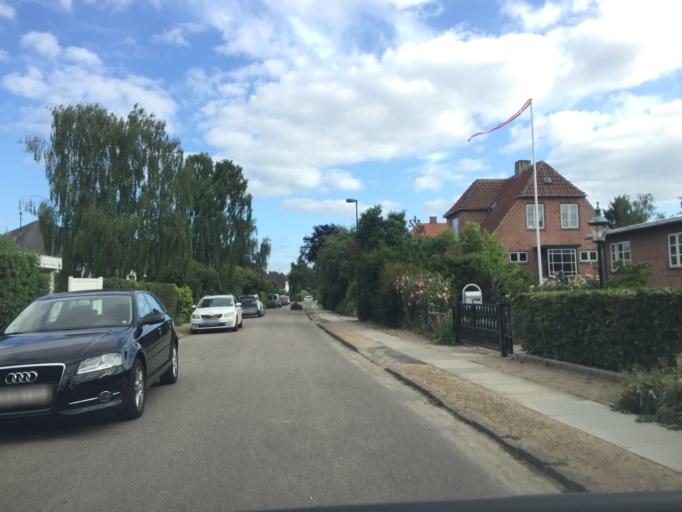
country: DK
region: Capital Region
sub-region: Kobenhavn
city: Vanlose
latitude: 55.6763
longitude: 12.4909
